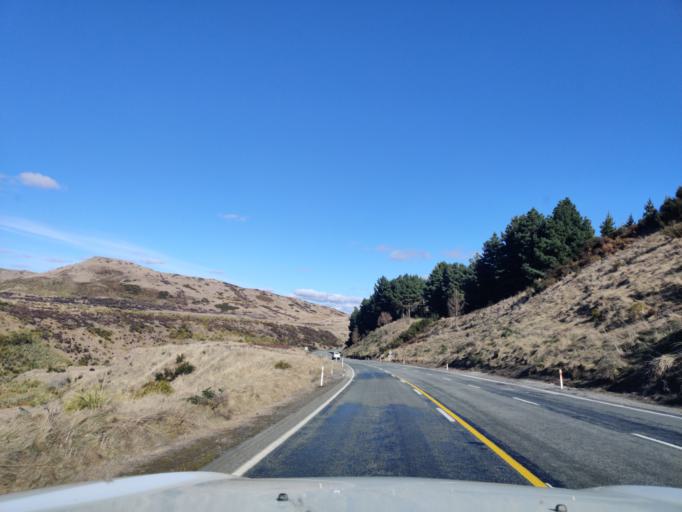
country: NZ
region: Manawatu-Wanganui
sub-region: Ruapehu District
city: Waiouru
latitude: -39.4397
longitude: 175.6816
